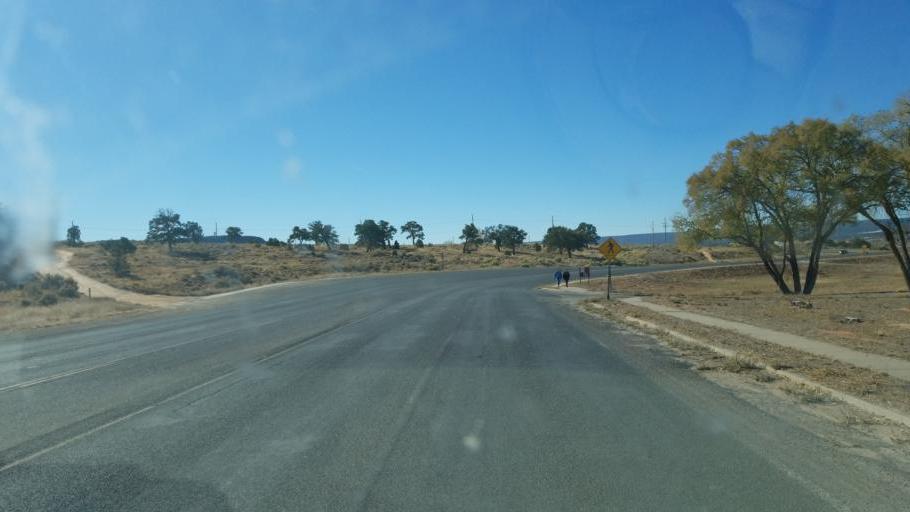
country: US
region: Arizona
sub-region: Apache County
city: Window Rock
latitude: 35.6732
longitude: -109.0566
